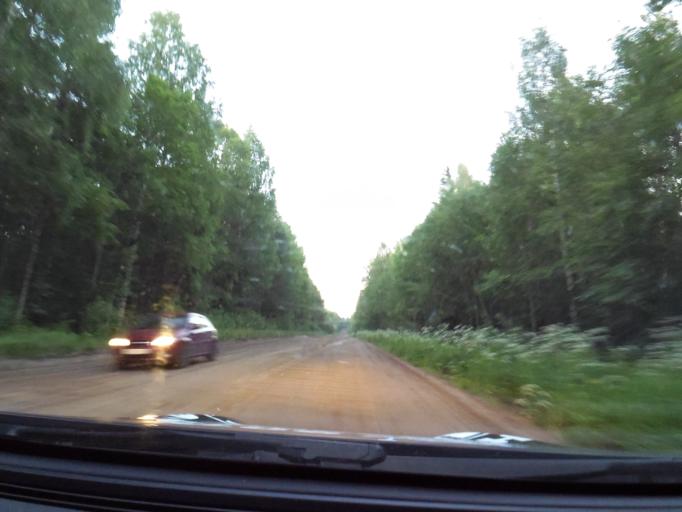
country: RU
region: Leningrad
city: Voznesen'ye
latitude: 60.8536
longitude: 35.8929
